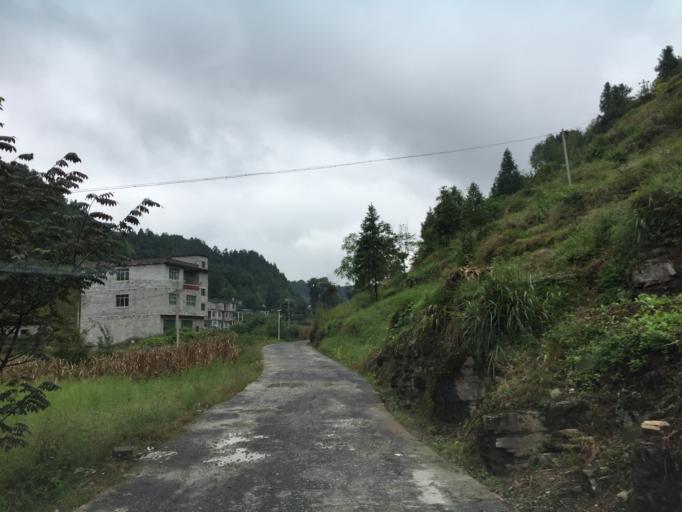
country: CN
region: Guizhou Sheng
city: Longquan
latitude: 28.2035
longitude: 108.0540
